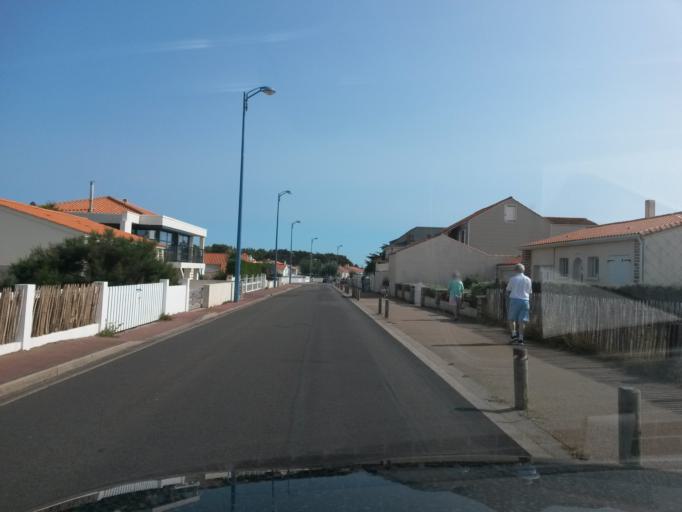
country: FR
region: Pays de la Loire
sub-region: Departement de la Vendee
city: Bretignolles-sur-Mer
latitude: 46.6226
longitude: -1.8729
